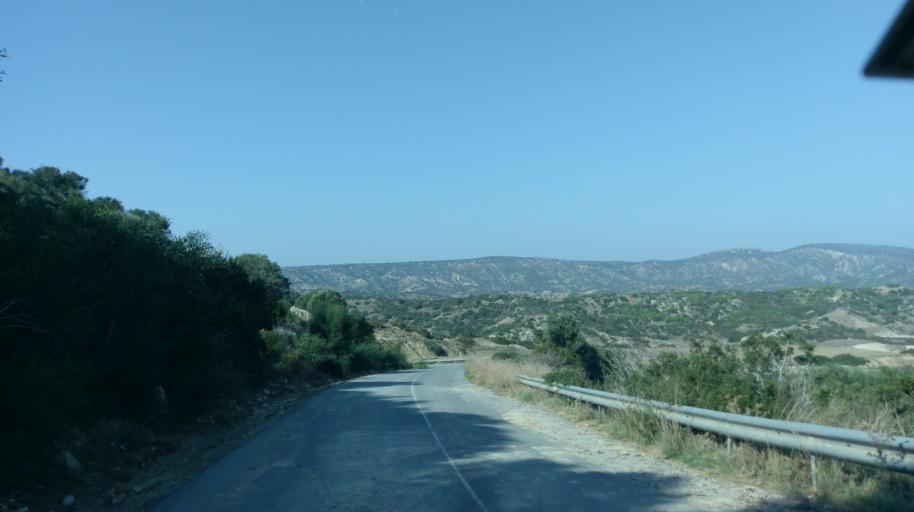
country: CY
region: Ammochostos
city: Leonarisso
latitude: 35.4949
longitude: 34.2261
